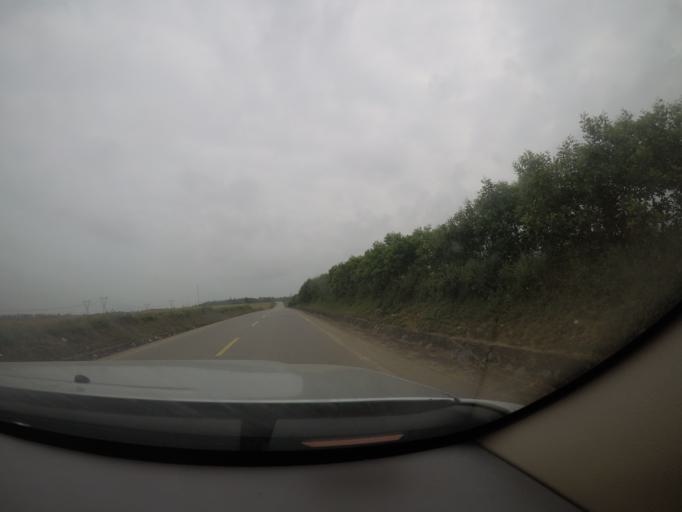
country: VN
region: Quang Binh
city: Hoan Lao
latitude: 17.5144
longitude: 106.4917
